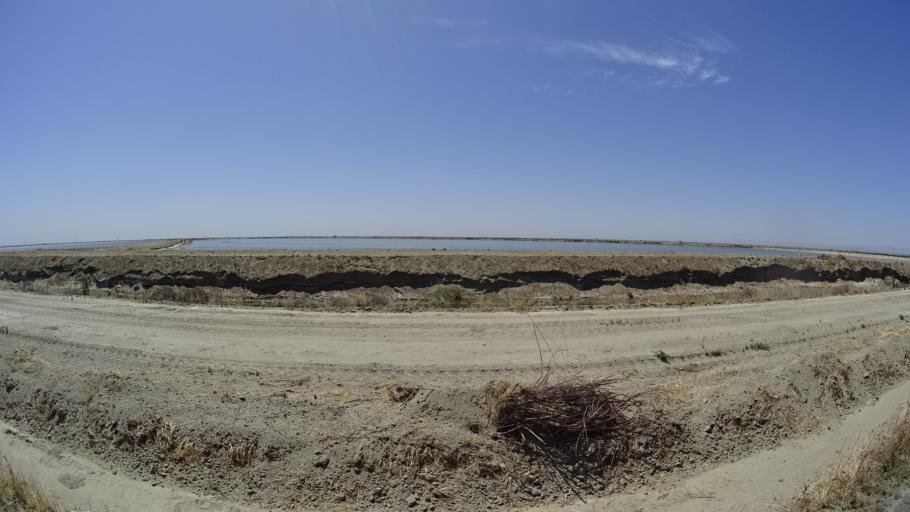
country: US
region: California
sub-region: Kings County
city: Stratford
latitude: 36.1379
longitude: -119.7041
